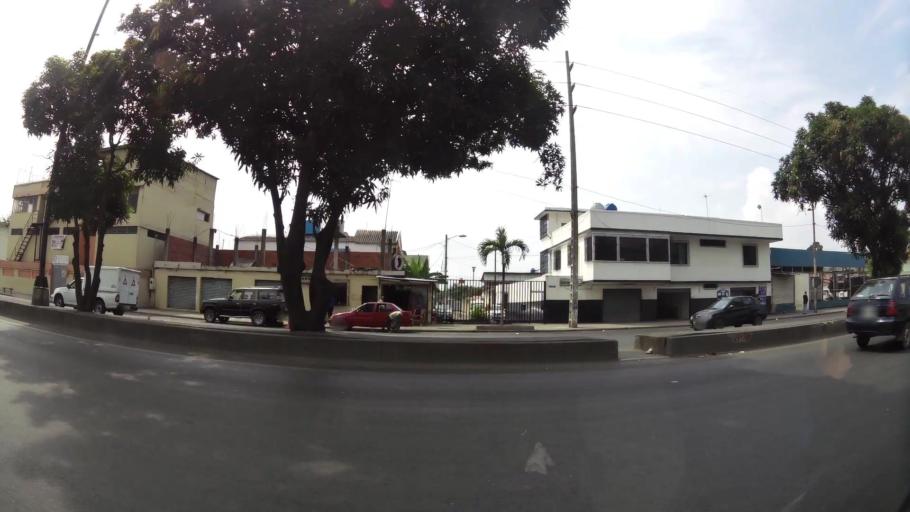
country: EC
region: Guayas
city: Guayaquil
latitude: -2.2391
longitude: -79.9032
